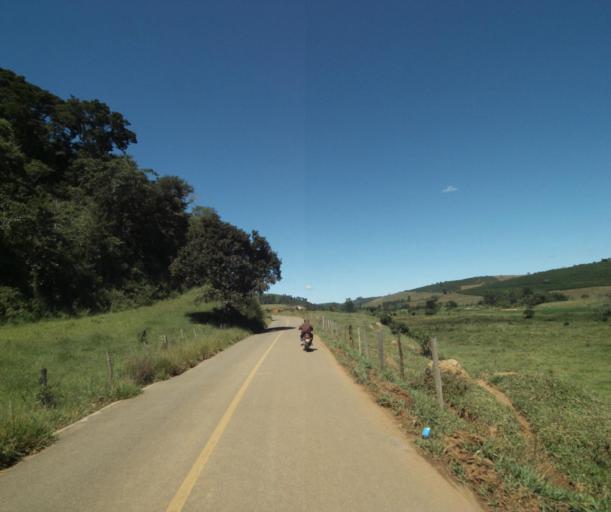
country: BR
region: Minas Gerais
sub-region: Espera Feliz
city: Espera Feliz
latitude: -20.5808
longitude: -41.8362
